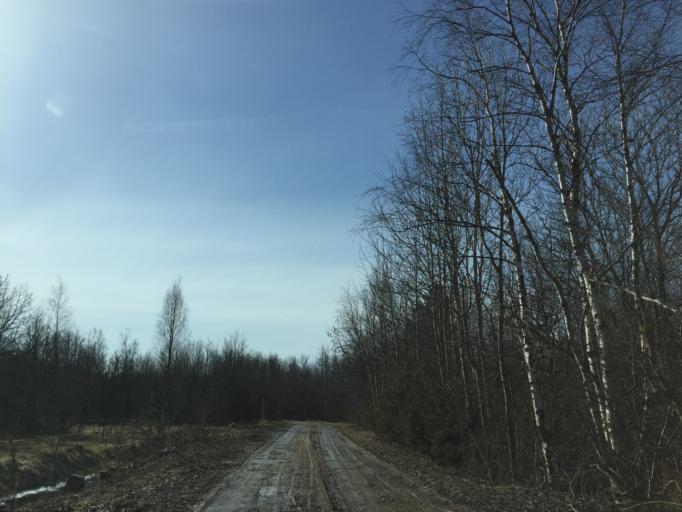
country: EE
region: Laeaene
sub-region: Haapsalu linn
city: Haapsalu
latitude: 58.6578
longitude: 23.5138
